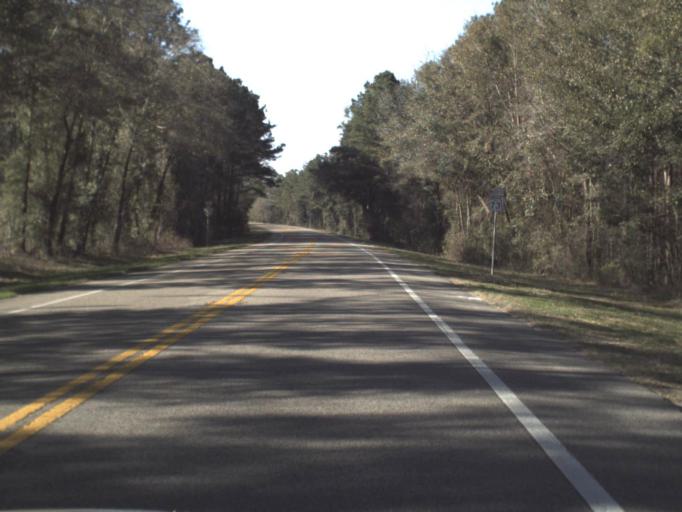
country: US
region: Florida
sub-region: Jackson County
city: Marianna
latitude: 30.6252
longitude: -85.1816
